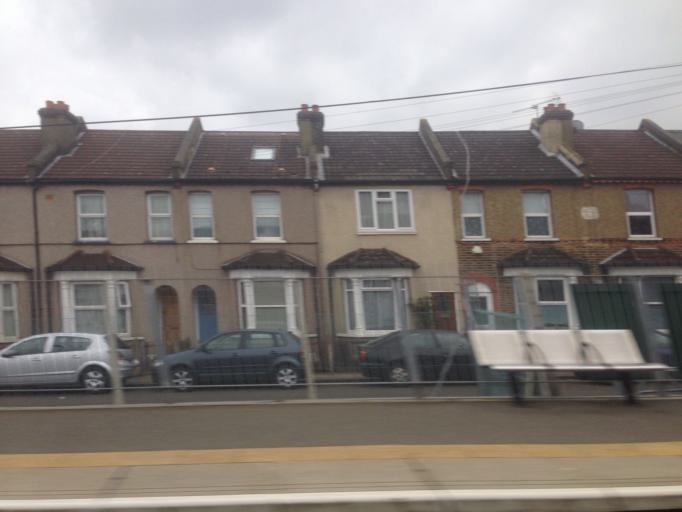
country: GB
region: England
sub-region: Greater London
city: Mitcham
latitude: 51.4062
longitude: -0.1556
